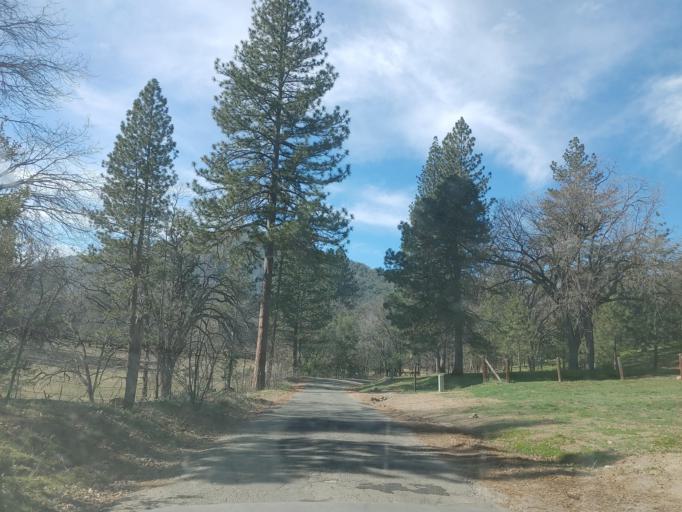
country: US
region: California
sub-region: Madera County
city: Ahwahnee
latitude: 37.4213
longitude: -119.7209
